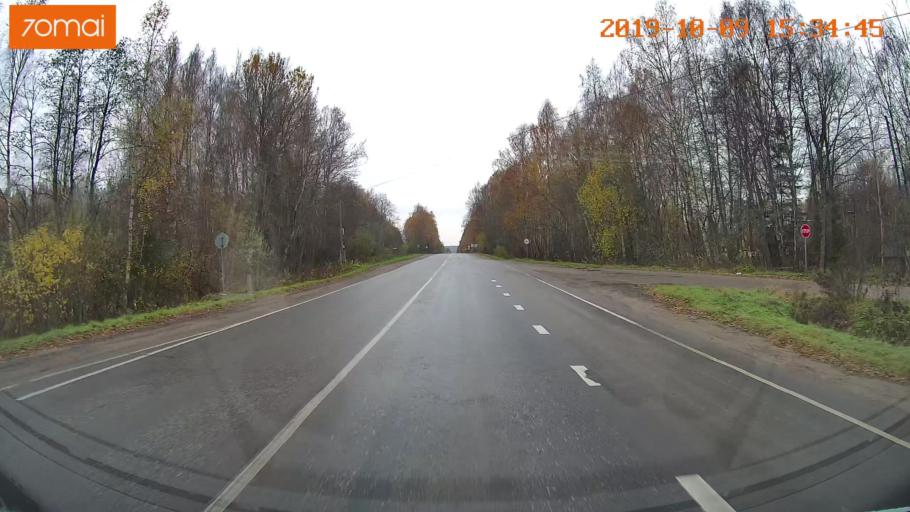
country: RU
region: Kostroma
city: Oktyabr'skiy
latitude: 57.9382
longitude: 41.2395
